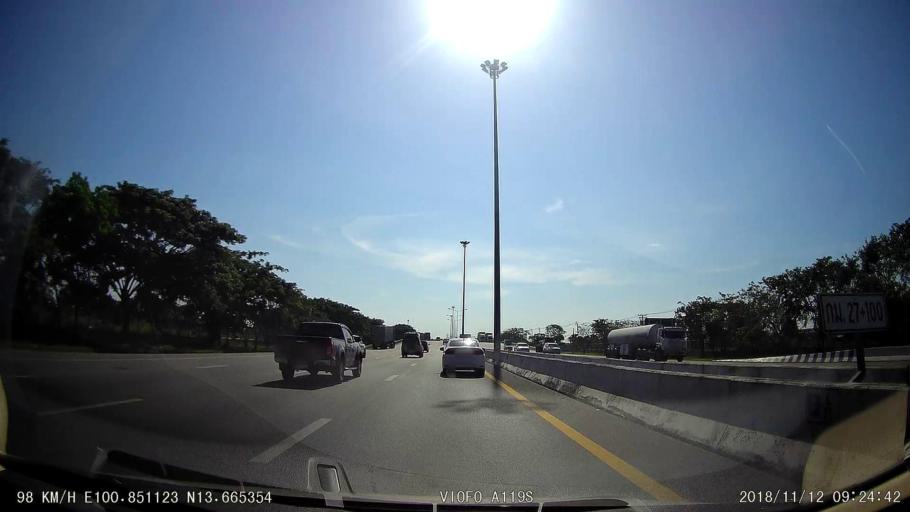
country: TH
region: Samut Prakan
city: Ban Khlong Bang Sao Thong
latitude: 13.6647
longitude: 100.8521
